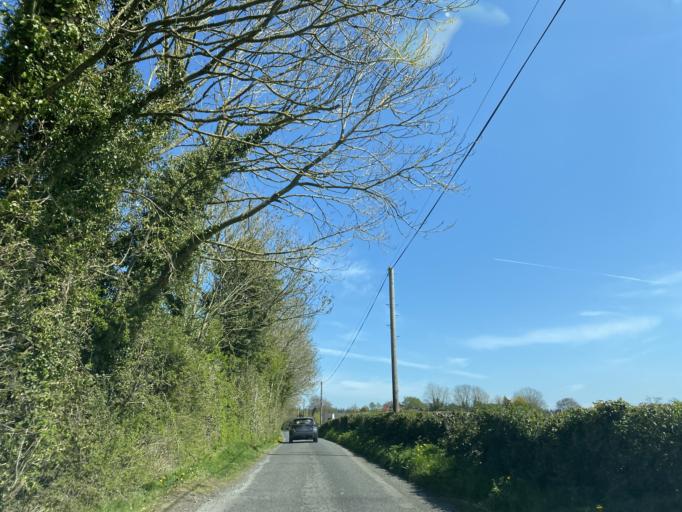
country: IE
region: Leinster
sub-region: Kildare
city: Rathangan
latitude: 53.2351
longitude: -7.0086
